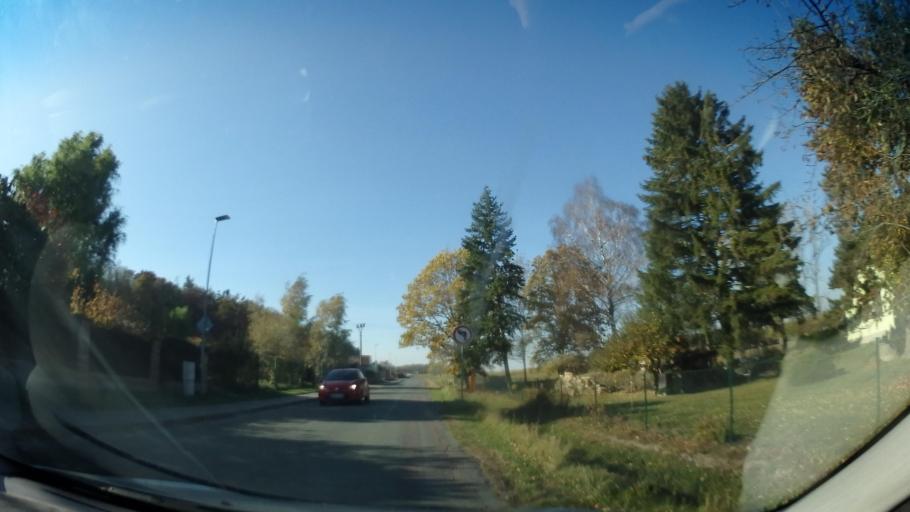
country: CZ
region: Kralovehradecky
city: Dolni Cernilov
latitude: 50.2486
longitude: 16.0086
